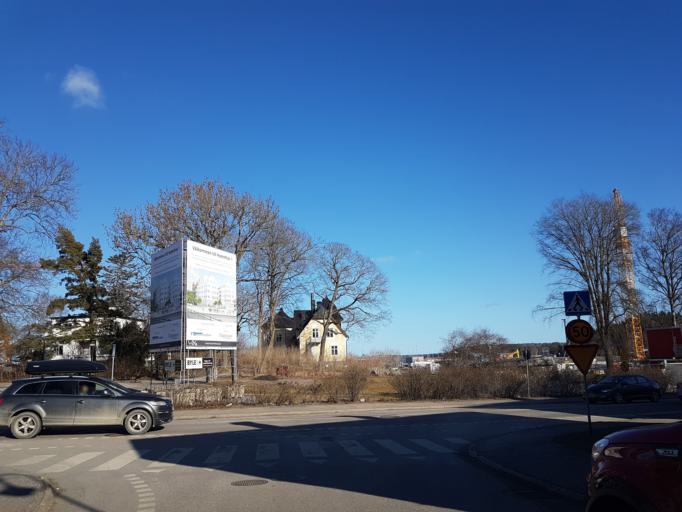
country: SE
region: Stockholm
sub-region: Norrtalje Kommun
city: Norrtalje
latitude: 59.7589
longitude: 18.7065
